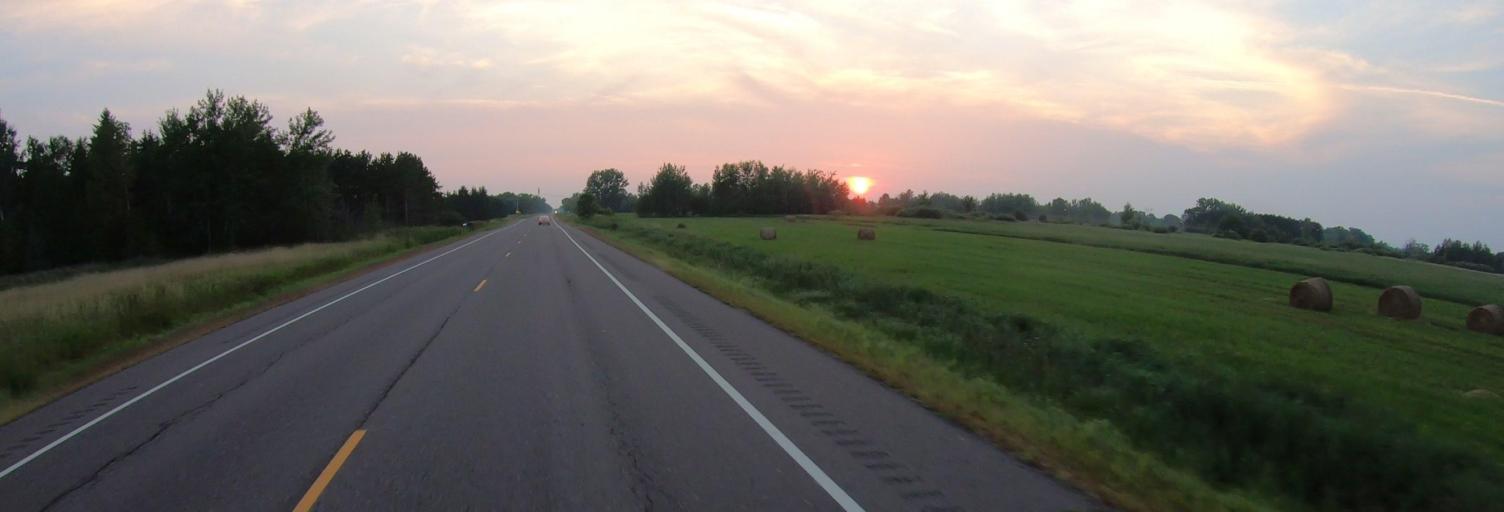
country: US
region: Minnesota
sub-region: Pine County
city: Rock Creek
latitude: 45.7735
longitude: -92.8934
